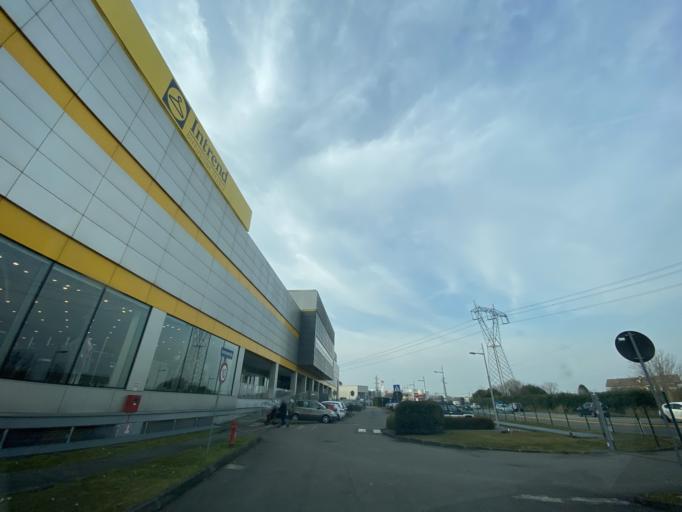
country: IT
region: Lombardy
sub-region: Citta metropolitana di Milano
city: Cernusco sul Naviglio
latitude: 45.5367
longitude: 9.3411
